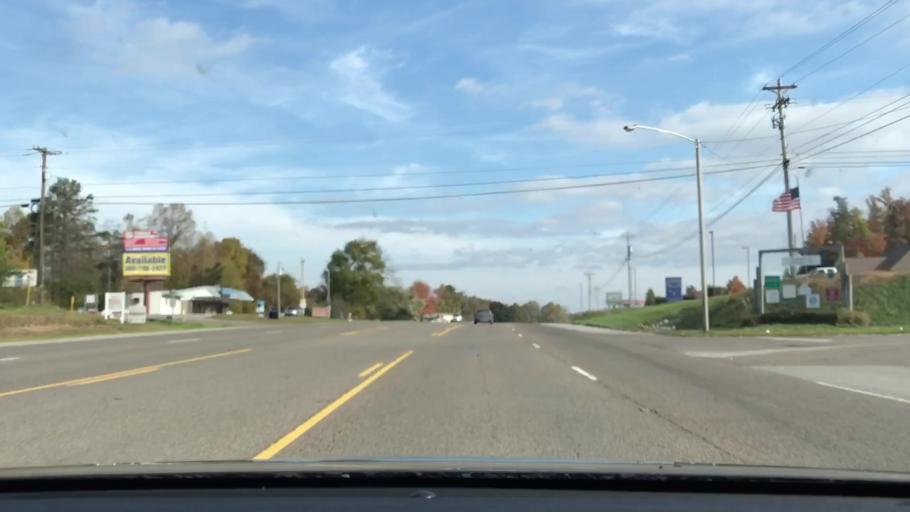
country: US
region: Tennessee
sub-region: Scott County
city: Oneida
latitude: 36.4698
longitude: -84.5451
